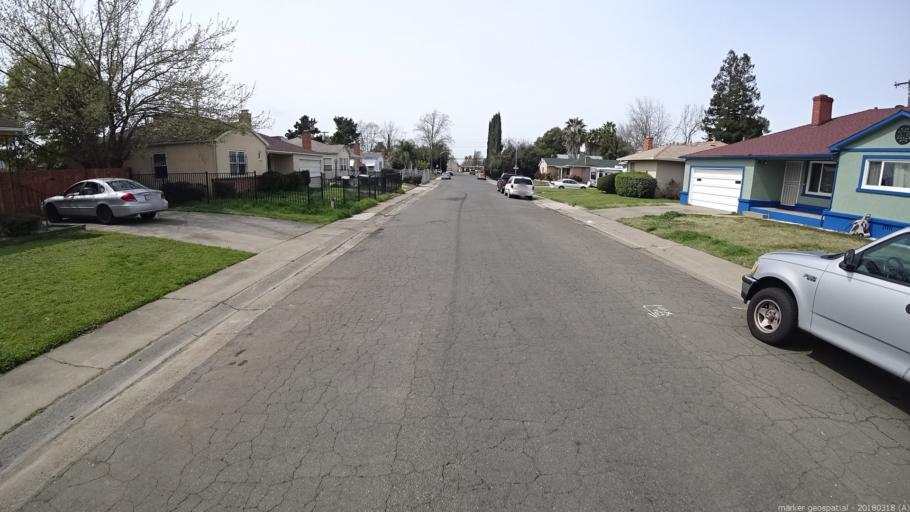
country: US
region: California
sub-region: Sacramento County
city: Parkway
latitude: 38.5186
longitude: -121.4537
